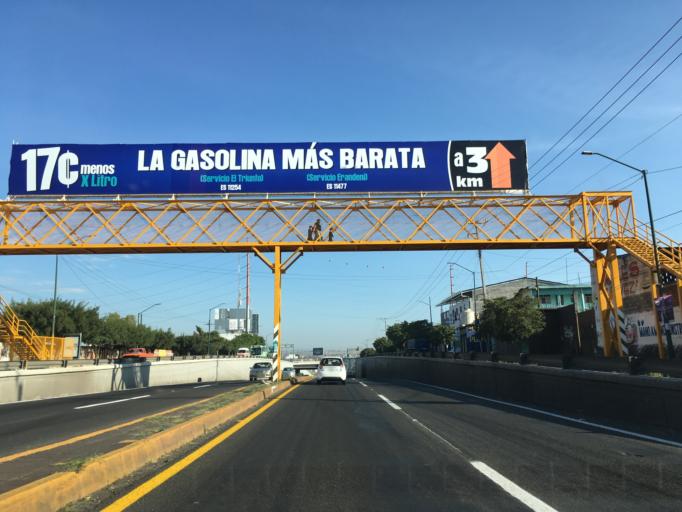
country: MX
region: Michoacan
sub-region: Tarimbaro
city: Fraccionamiento Privadas del Sol
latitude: 19.7302
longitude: -101.1830
